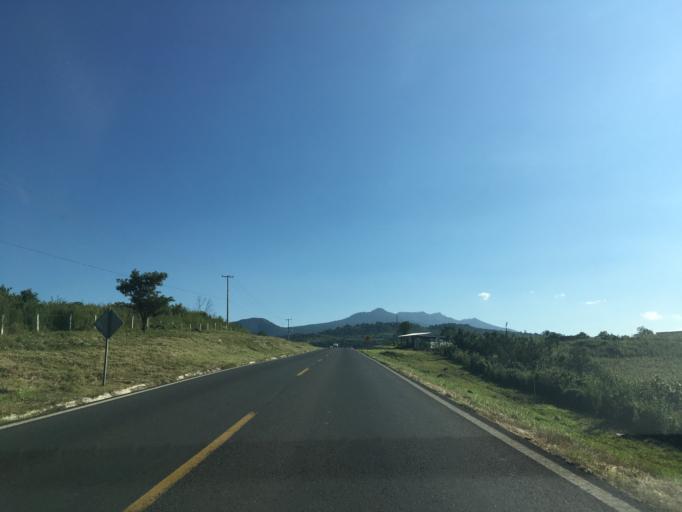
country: MX
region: Mexico
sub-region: Chalco
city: Los Nogales
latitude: 19.8559
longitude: -102.1368
